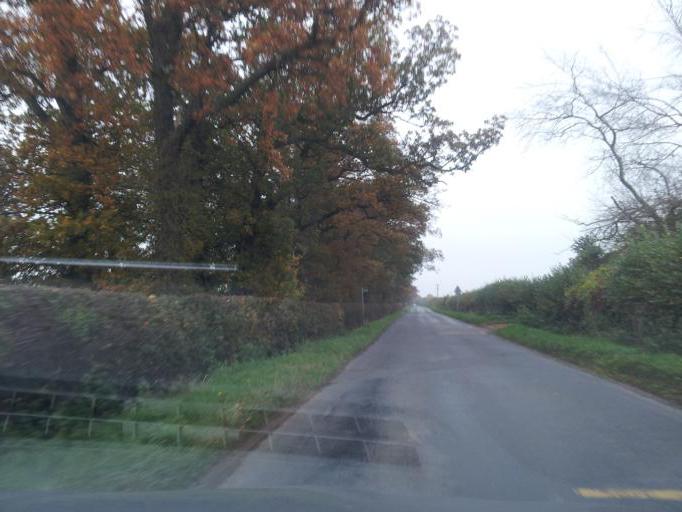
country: GB
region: England
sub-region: Milton Keynes
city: Shenley Church End
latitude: 51.9965
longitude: -0.8206
